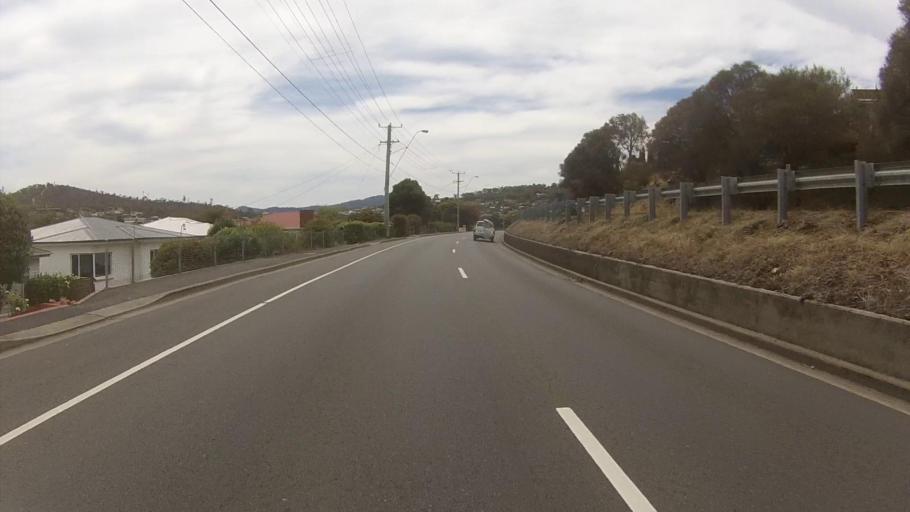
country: AU
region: Tasmania
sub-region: Clarence
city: Lindisfarne
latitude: -42.8553
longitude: 147.3567
